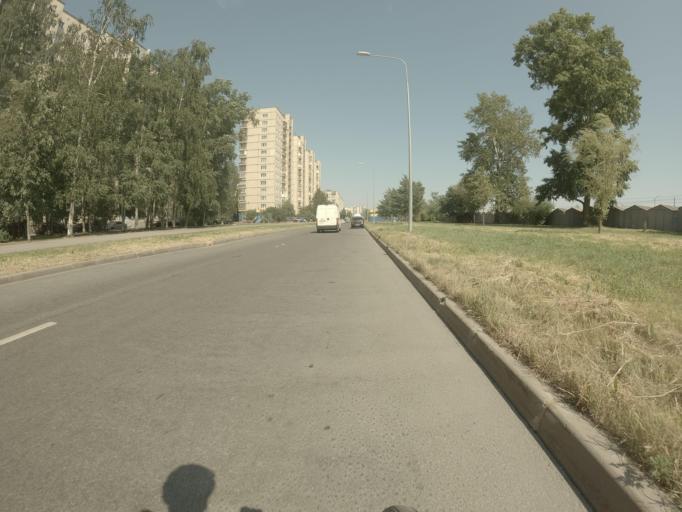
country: RU
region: St.-Petersburg
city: Krasnogvargeisky
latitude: 59.9372
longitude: 30.5009
